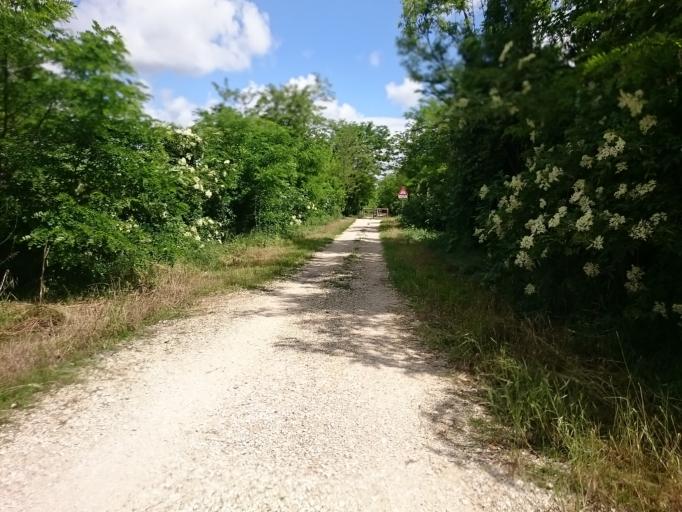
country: IT
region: Veneto
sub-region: Provincia di Padova
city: Campodoro
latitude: 45.4936
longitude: 11.7352
